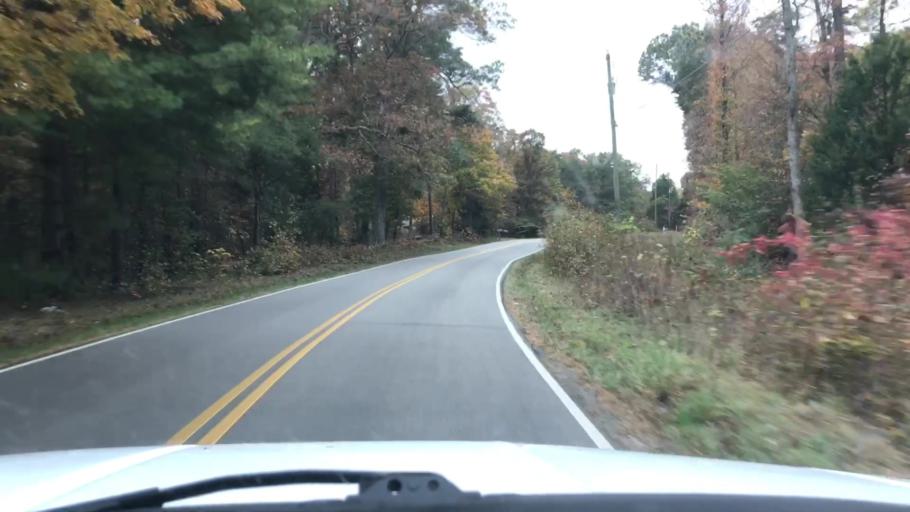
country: US
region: Virginia
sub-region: Goochland County
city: Goochland
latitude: 37.6847
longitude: -77.8676
